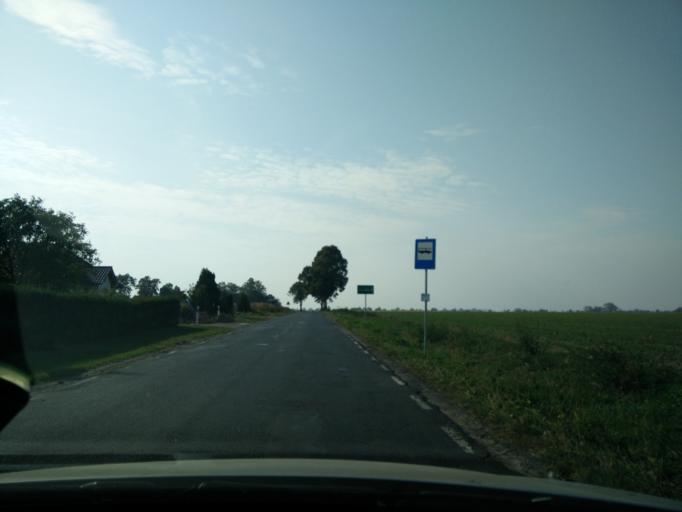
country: PL
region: Greater Poland Voivodeship
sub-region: Powiat sredzki
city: Sroda Wielkopolska
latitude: 52.2654
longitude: 17.3106
